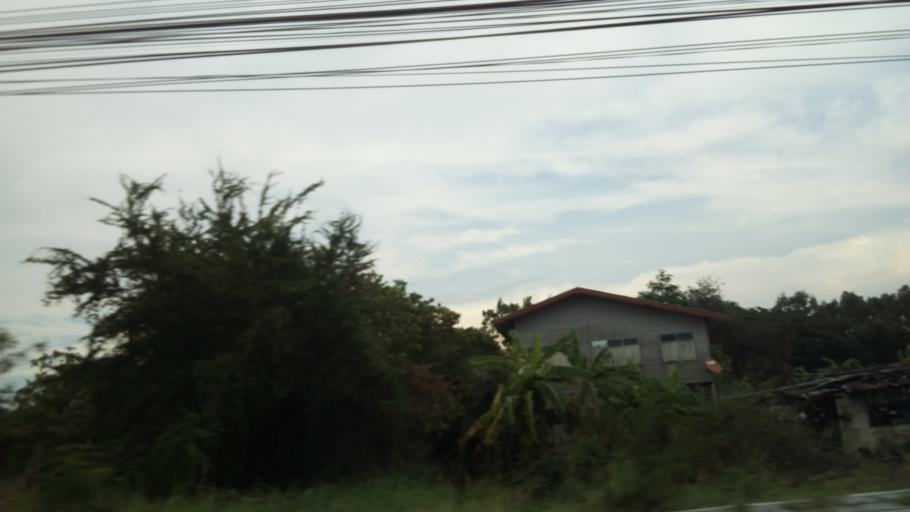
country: TH
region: Pathum Thani
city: Thanyaburi
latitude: 14.0479
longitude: 100.7099
